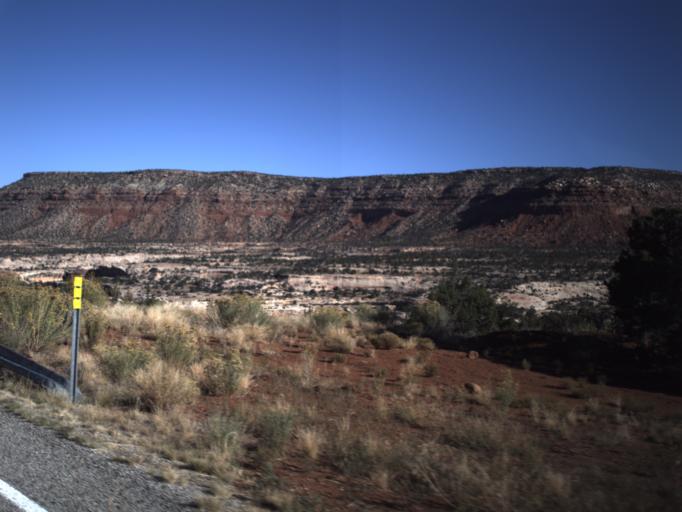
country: US
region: Utah
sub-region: San Juan County
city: Blanding
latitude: 37.5933
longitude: -110.0432
